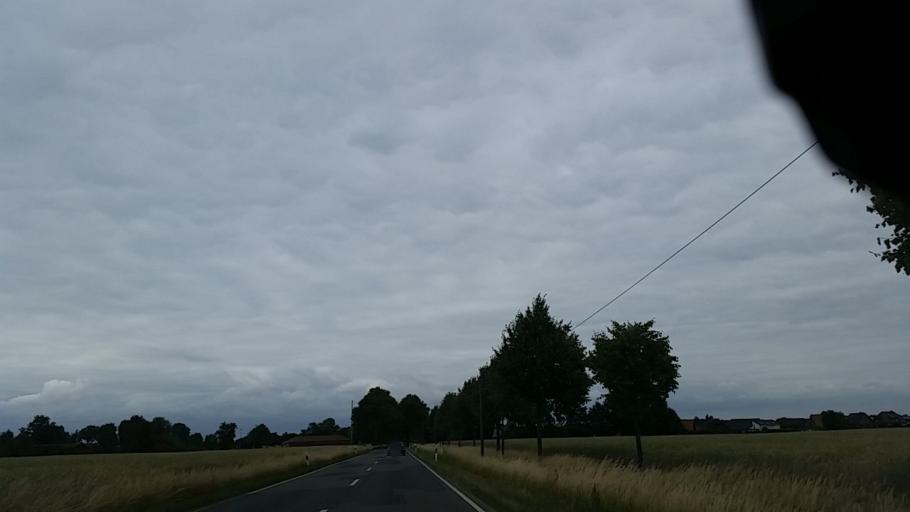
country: DE
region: Lower Saxony
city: Grafhorst
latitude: 52.4395
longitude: 10.9366
